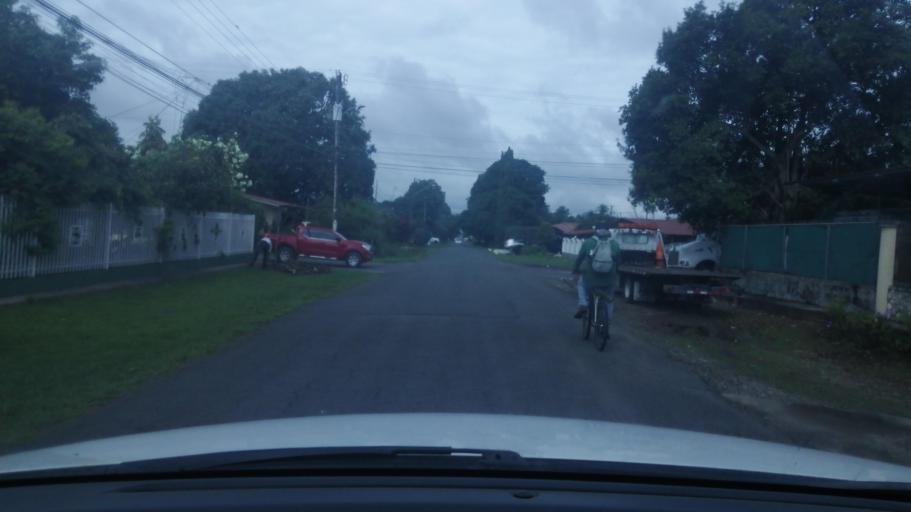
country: PA
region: Chiriqui
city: David
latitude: 8.4357
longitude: -82.4306
